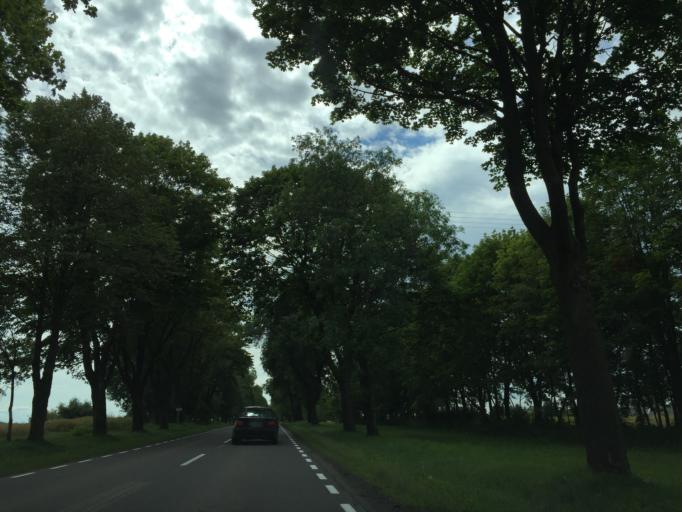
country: PL
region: Podlasie
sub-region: Powiat bielski
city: Bocki
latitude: 52.6682
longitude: 23.0939
